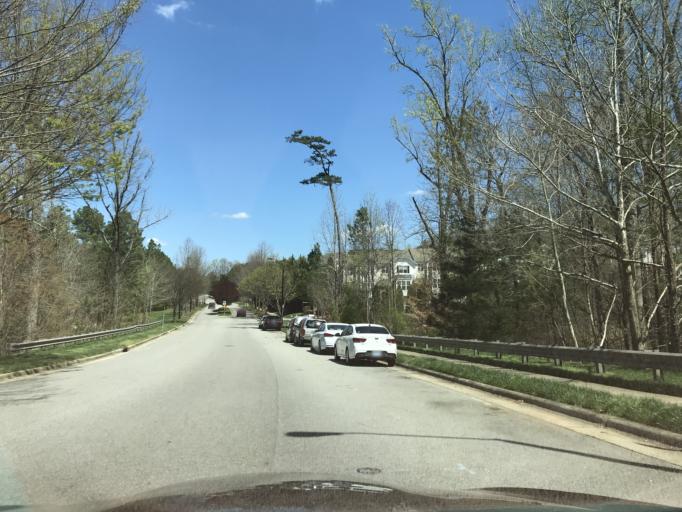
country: US
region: North Carolina
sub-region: Wake County
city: West Raleigh
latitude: 35.8619
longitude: -78.7190
